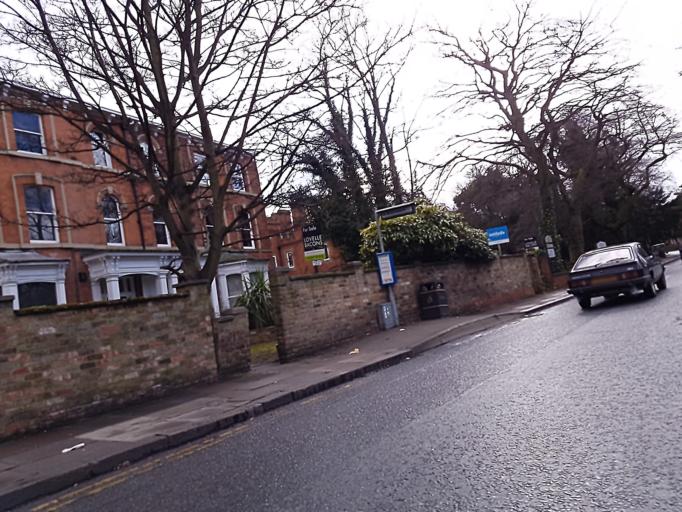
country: GB
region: England
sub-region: North East Lincolnshire
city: Grimbsy
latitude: 53.5617
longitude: -0.0921
